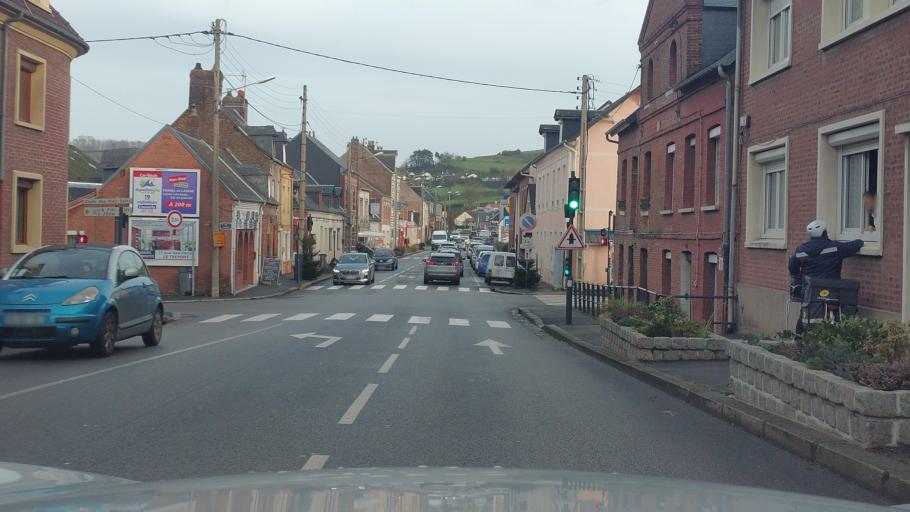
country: FR
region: Haute-Normandie
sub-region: Departement de la Seine-Maritime
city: Eu
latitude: 50.0539
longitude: 1.4224
